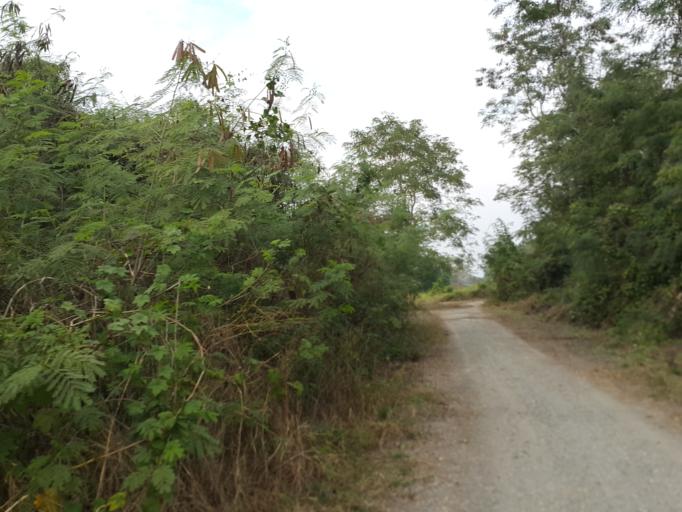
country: TH
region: Chiang Mai
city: San Kamphaeng
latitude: 18.8011
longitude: 99.1186
